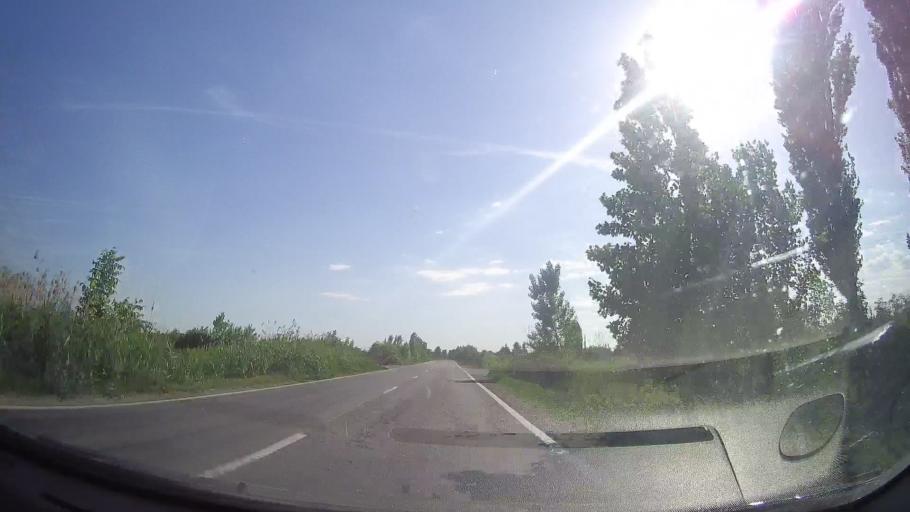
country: RO
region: Prahova
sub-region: Comuna Barcanesti
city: Barcanesti
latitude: 44.8964
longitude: 26.0566
